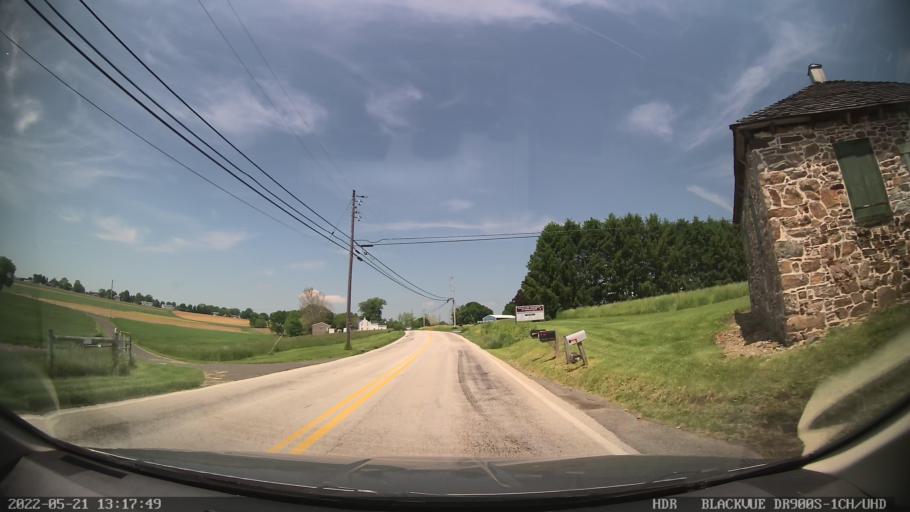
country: US
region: Pennsylvania
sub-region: Berks County
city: Bally
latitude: 40.3626
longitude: -75.5918
